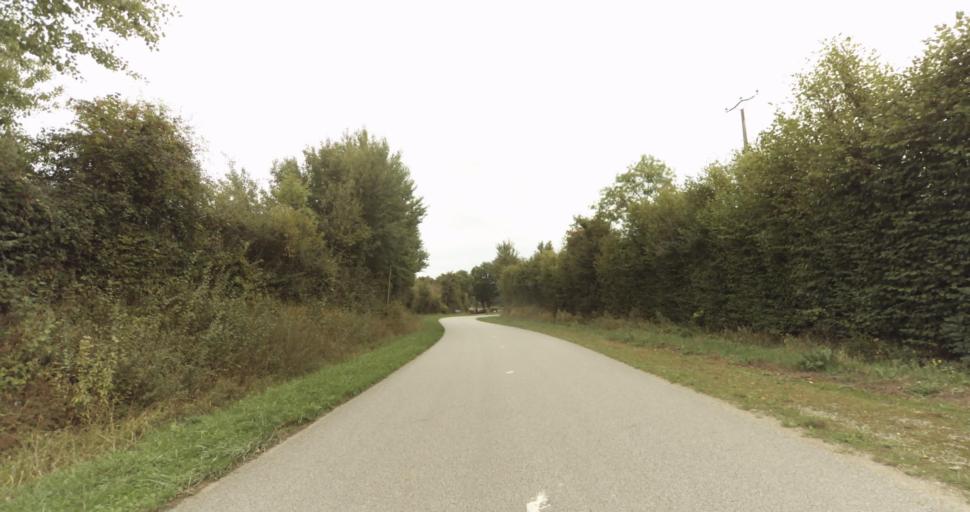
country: FR
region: Lower Normandy
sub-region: Departement de l'Orne
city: Sees
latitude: 48.6809
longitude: 0.2474
